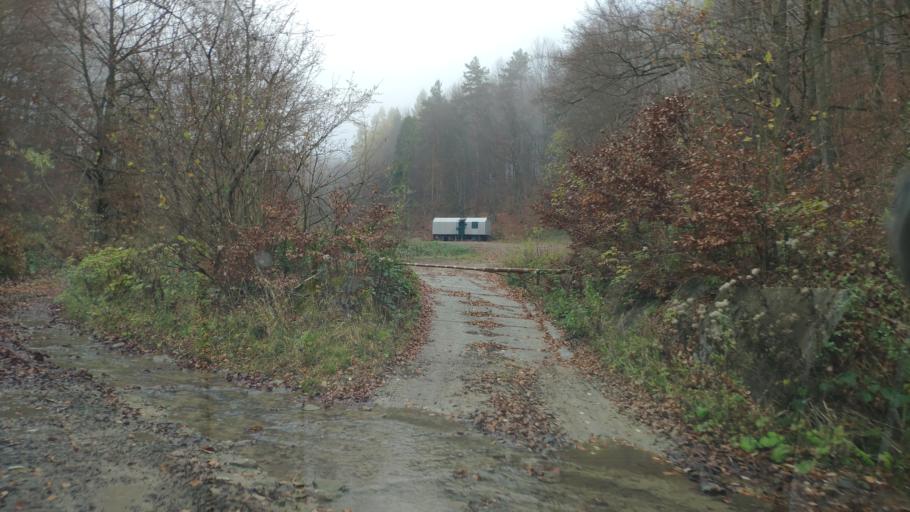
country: SK
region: Presovsky
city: Sabinov
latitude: 49.1575
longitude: 21.2015
